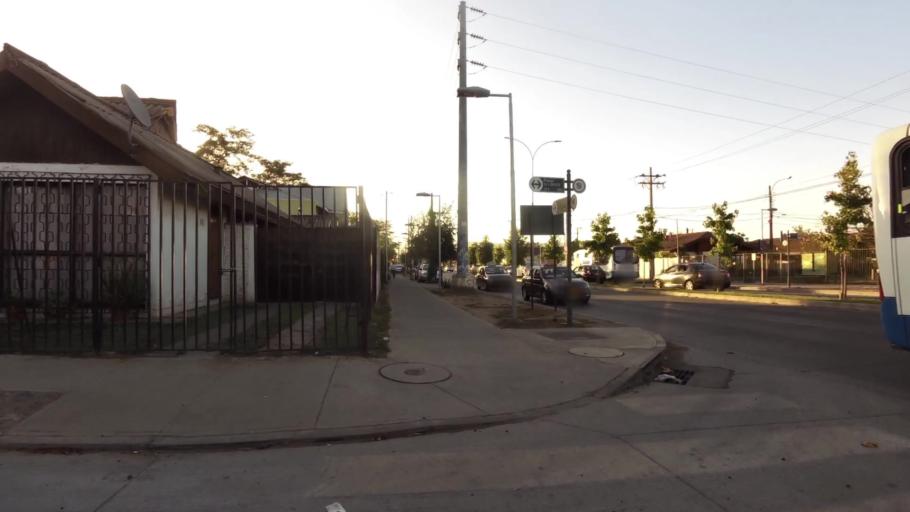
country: CL
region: Maule
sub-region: Provincia de Talca
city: Talca
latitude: -35.4379
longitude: -71.6406
